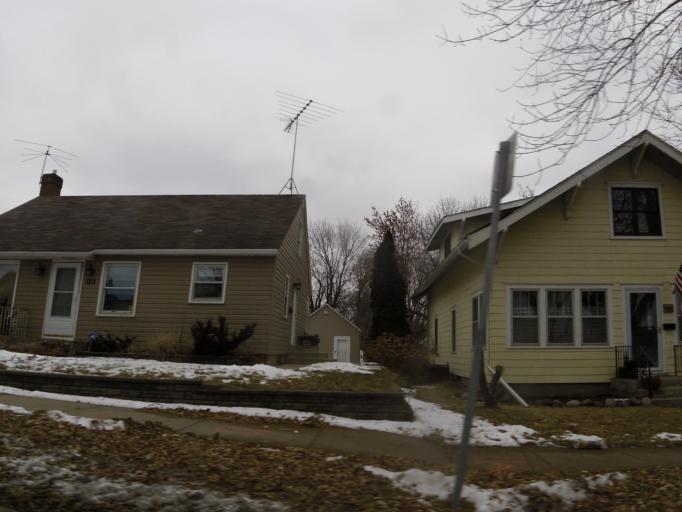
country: US
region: Minnesota
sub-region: Carver County
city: Waconia
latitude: 44.8450
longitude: -93.7877
